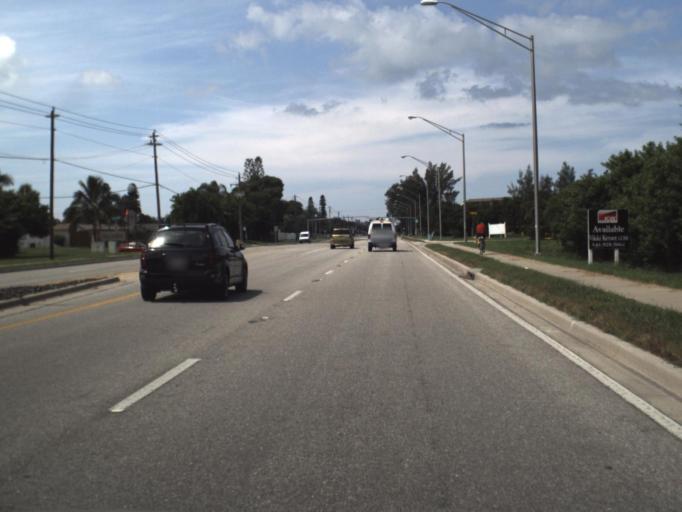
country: US
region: Florida
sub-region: Manatee County
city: Cortez
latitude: 27.4618
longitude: -82.6536
